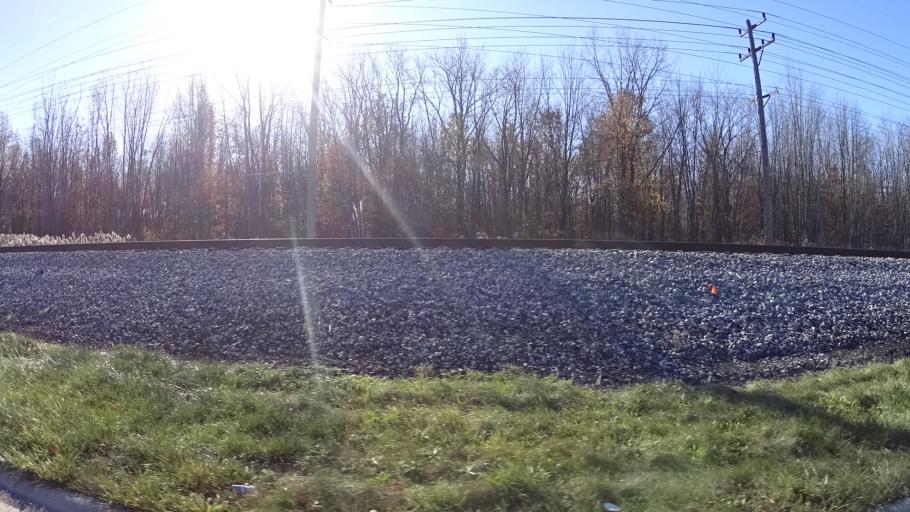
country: US
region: Ohio
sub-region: Lorain County
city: Avon Center
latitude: 41.4783
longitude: -81.9864
